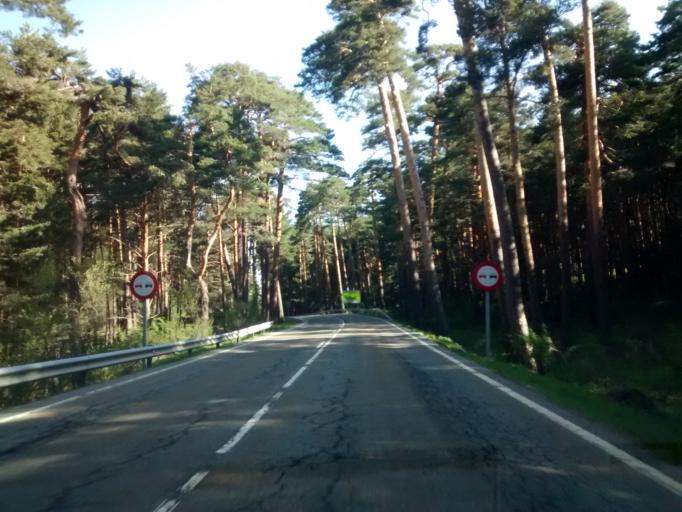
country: ES
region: Castille and Leon
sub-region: Provincia de Segovia
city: San Ildefonso
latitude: 40.8285
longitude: -4.0227
